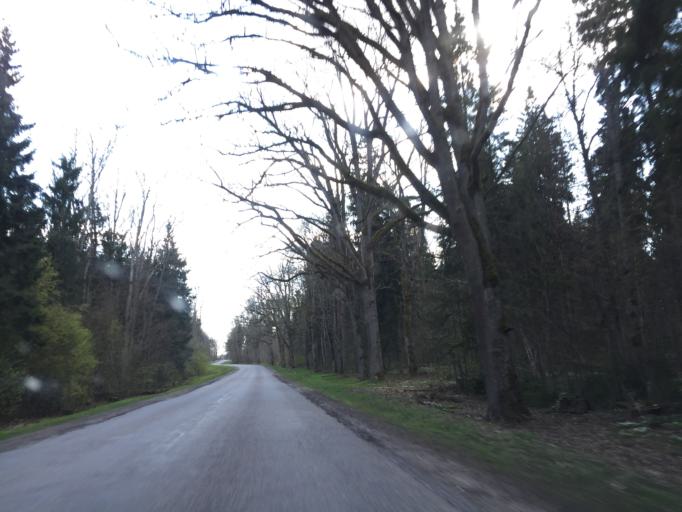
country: LV
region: Krimulda
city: Ragana
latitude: 57.3380
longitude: 24.6521
